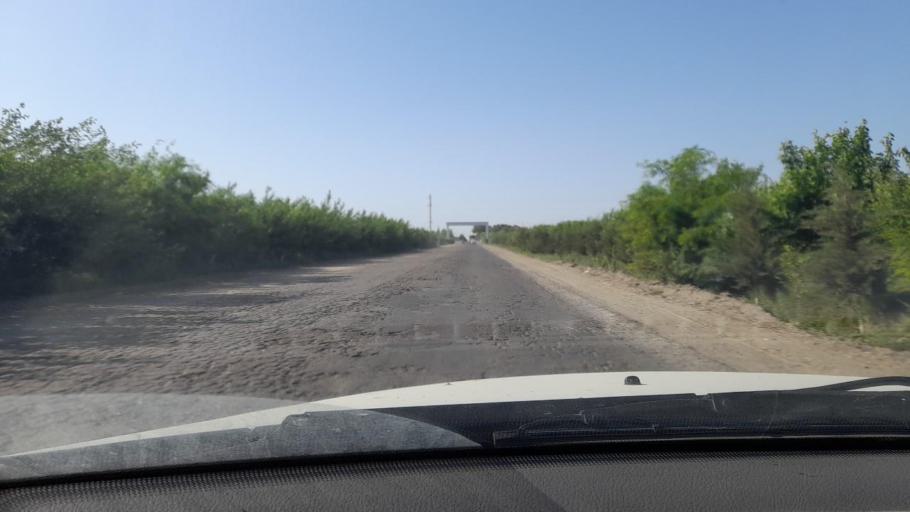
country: UZ
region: Bukhara
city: Romiton
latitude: 40.0674
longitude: 64.3269
